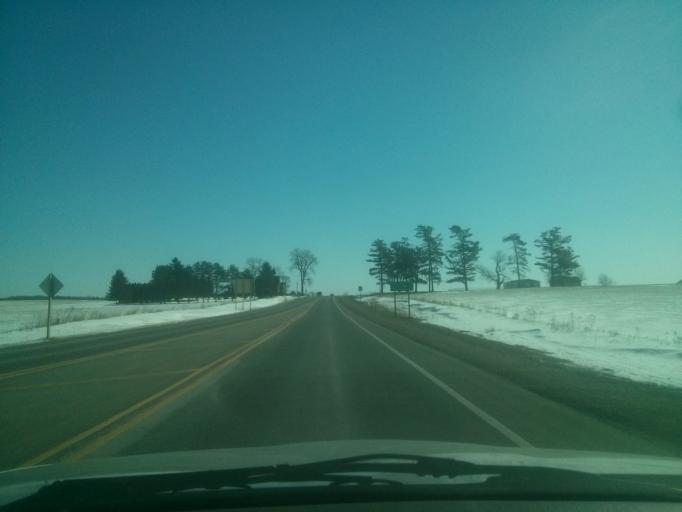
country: US
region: Wisconsin
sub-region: Saint Croix County
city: New Richmond
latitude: 45.1365
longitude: -92.3812
